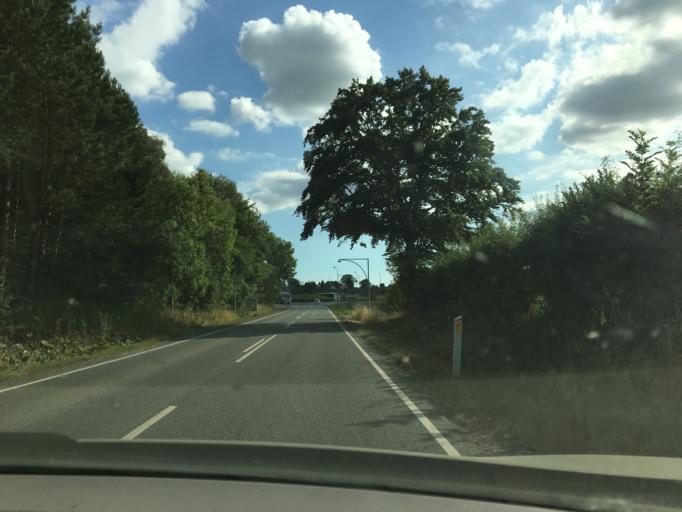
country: DK
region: South Denmark
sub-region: Nordfyns Kommune
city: Sonderso
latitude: 55.4509
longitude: 10.1868
